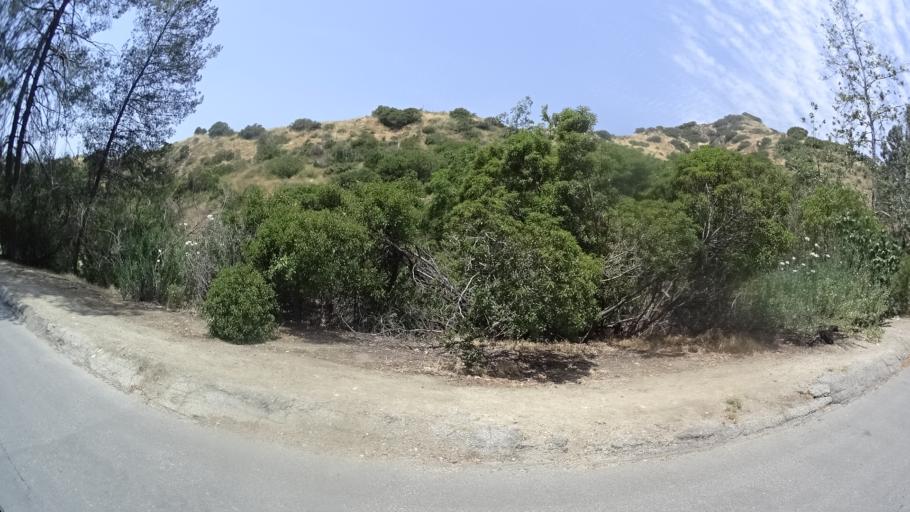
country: US
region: California
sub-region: Los Angeles County
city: Burbank
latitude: 34.2042
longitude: -118.2957
